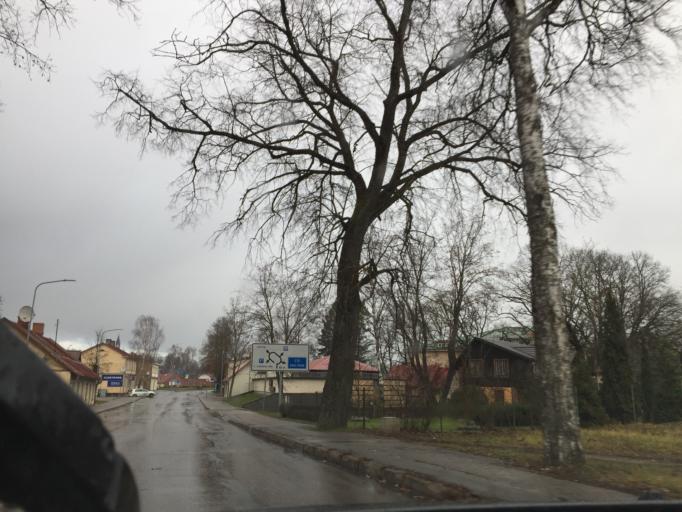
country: LV
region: Valmieras Rajons
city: Valmiera
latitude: 57.5323
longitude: 25.4248
